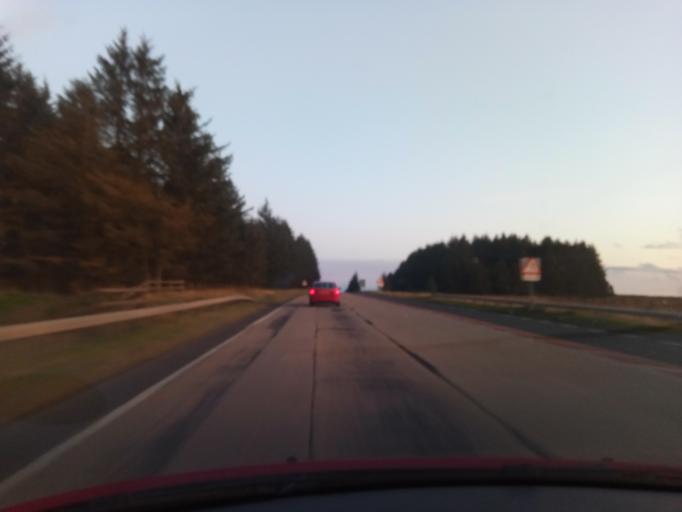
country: GB
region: Scotland
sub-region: East Lothian
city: Pencaitland
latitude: 55.8093
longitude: -2.8388
